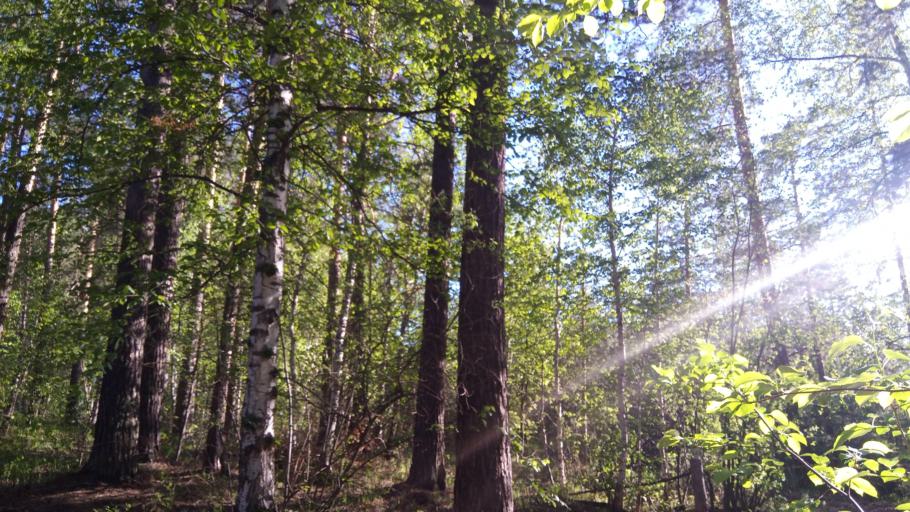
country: RU
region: Chelyabinsk
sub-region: Gorod Chelyabinsk
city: Chelyabinsk
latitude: 55.1383
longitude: 61.3382
